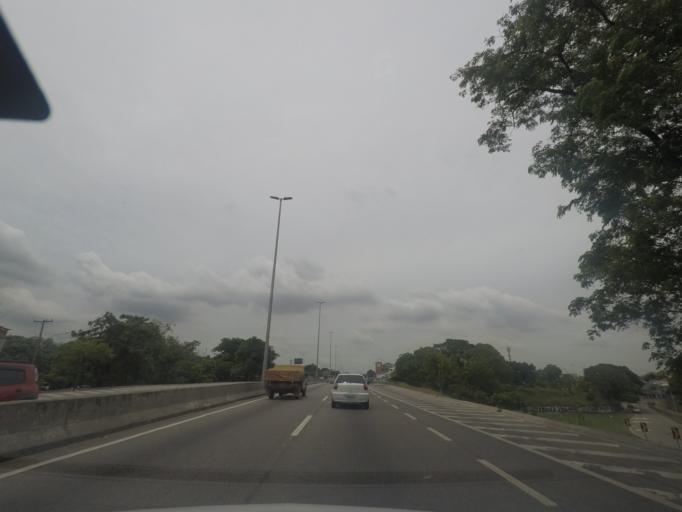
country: BR
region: Rio de Janeiro
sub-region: Rio De Janeiro
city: Rio de Janeiro
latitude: -22.8699
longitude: -43.2443
